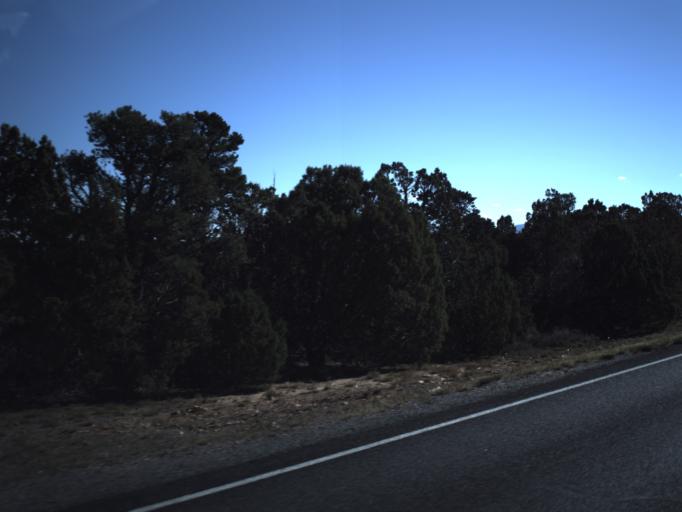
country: US
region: Utah
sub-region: Iron County
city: Cedar City
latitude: 37.6092
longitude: -113.3685
